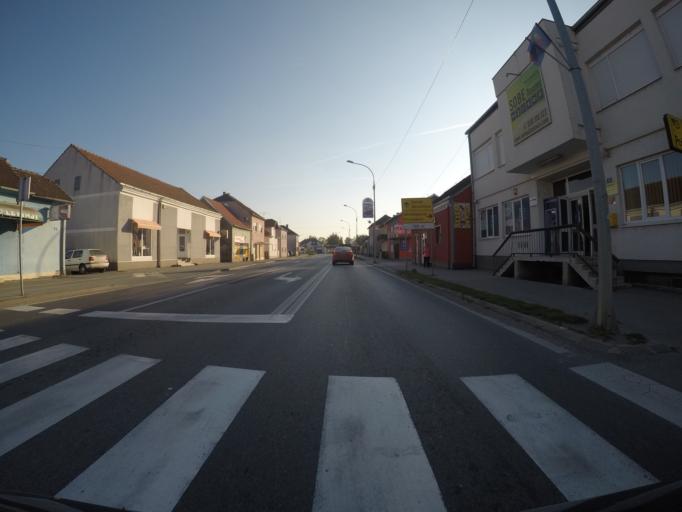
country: HR
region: Virovitick-Podravska
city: Pitomaca
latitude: 45.9486
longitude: 17.2321
